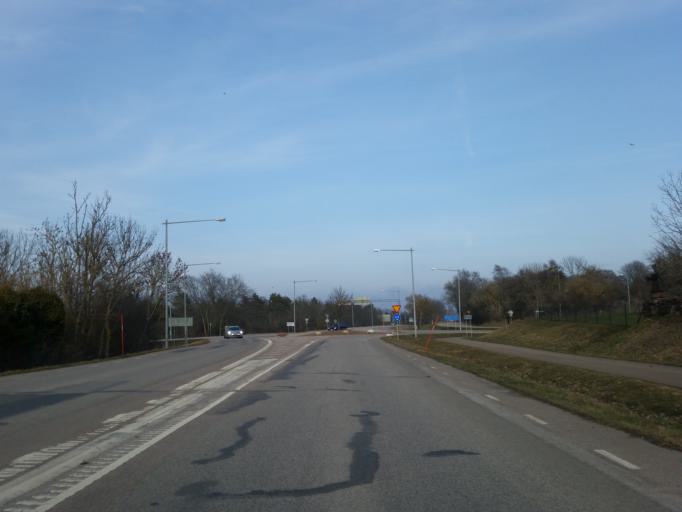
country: SE
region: Kalmar
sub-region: Borgholms Kommun
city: Borgholm
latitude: 56.8769
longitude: 16.6779
